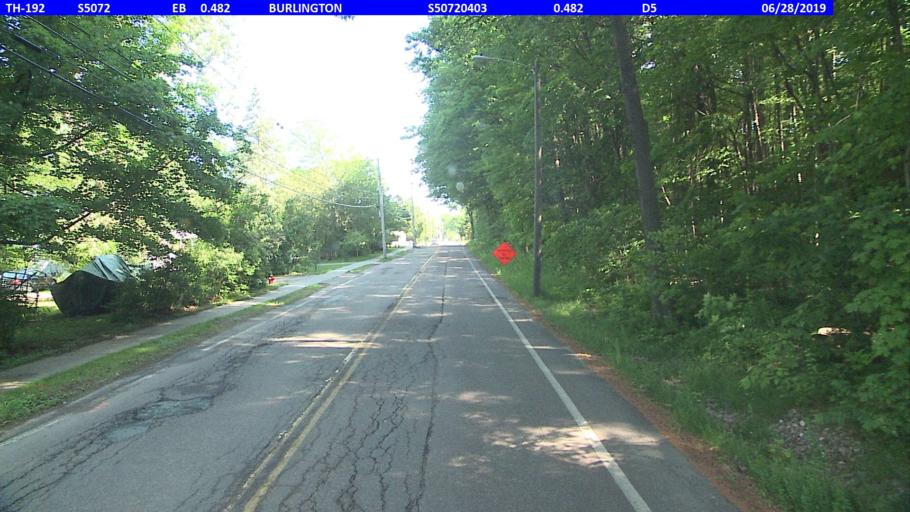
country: US
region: Vermont
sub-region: Chittenden County
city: Burlington
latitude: 44.5106
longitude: -73.2417
